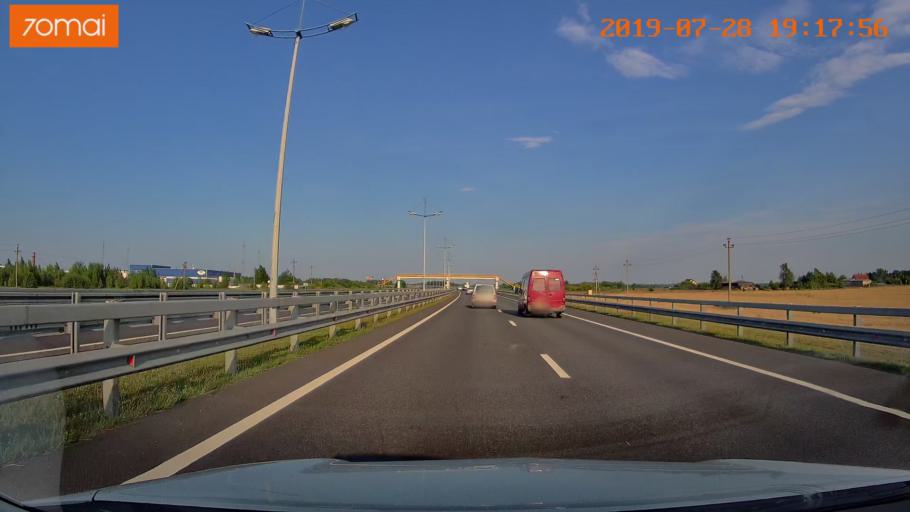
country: RU
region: Kaliningrad
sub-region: Zelenogradskiy Rayon
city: Zelenogradsk
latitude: 54.9197
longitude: 20.4168
